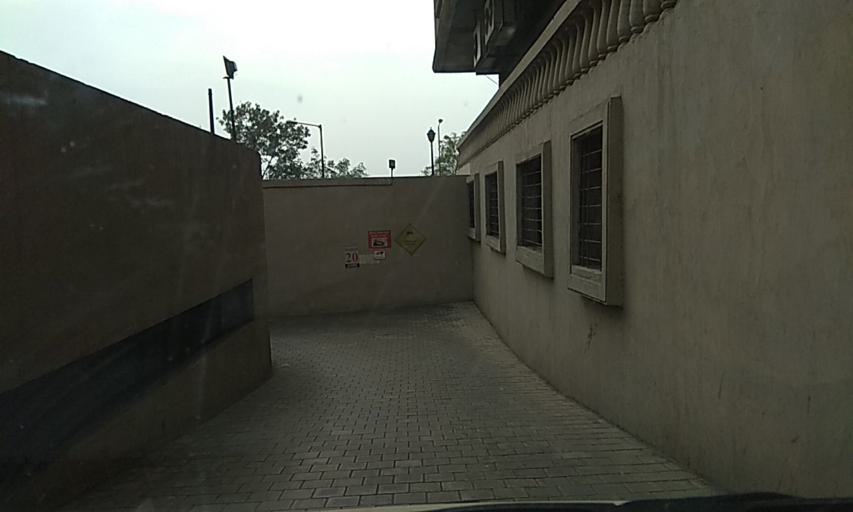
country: IN
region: Maharashtra
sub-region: Pune Division
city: Lohogaon
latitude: 18.5445
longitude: 73.9106
